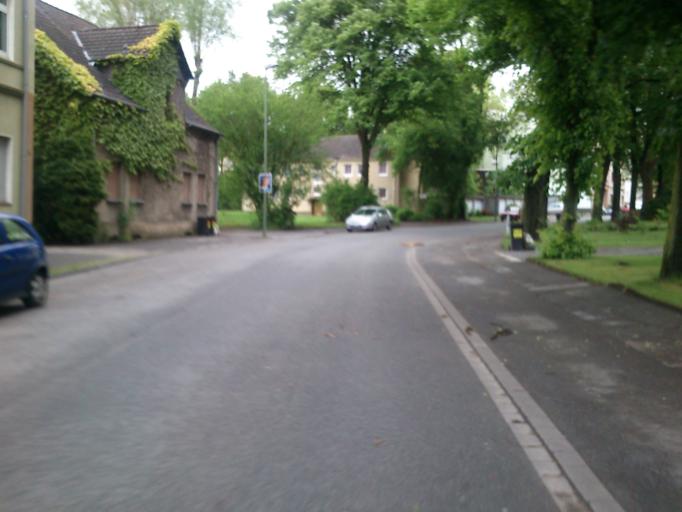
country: DE
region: North Rhine-Westphalia
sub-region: Regierungsbezirk Arnsberg
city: Herne
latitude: 51.5193
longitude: 7.2172
